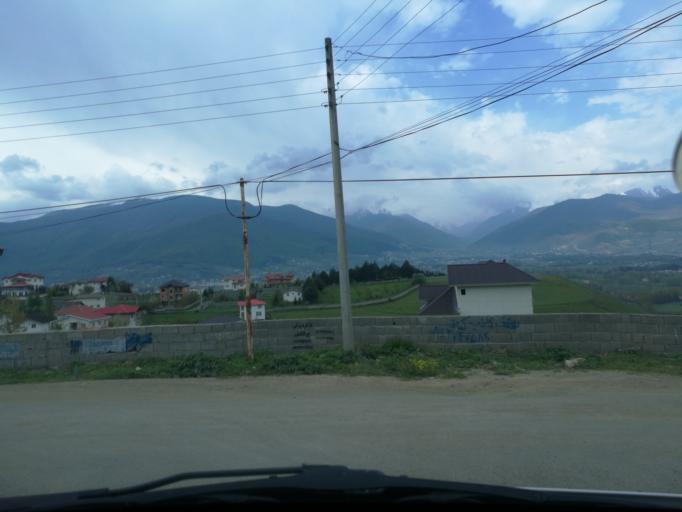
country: IR
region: Mazandaran
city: `Abbasabad
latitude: 36.5343
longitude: 51.2234
